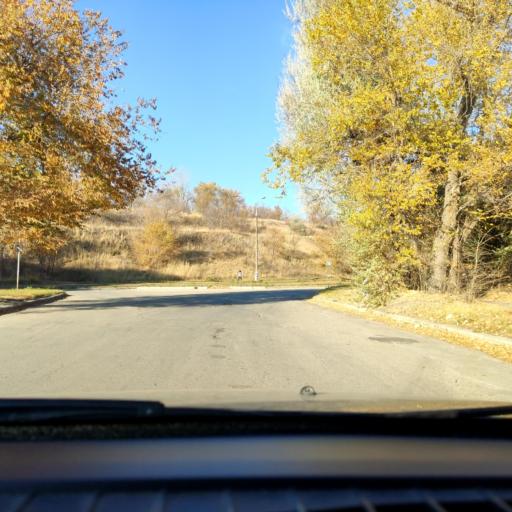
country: RU
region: Samara
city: Tol'yatti
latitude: 53.4964
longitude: 49.2679
